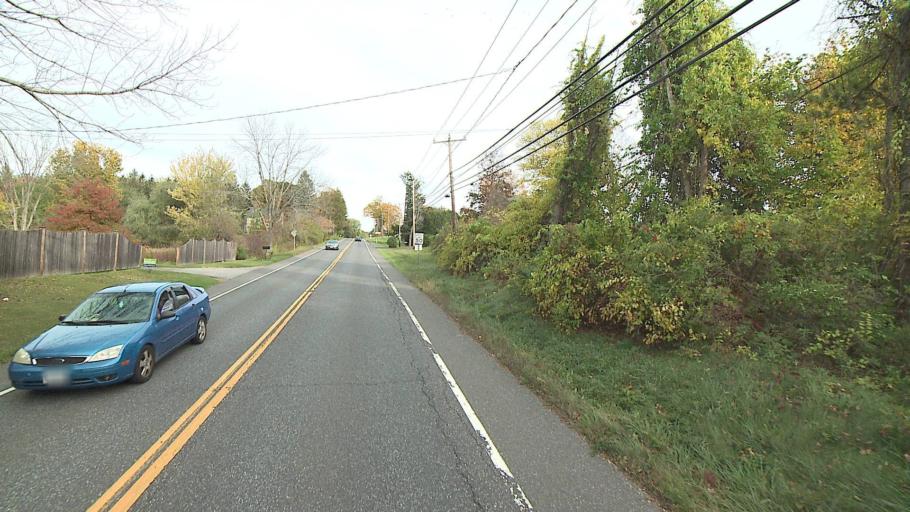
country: US
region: Connecticut
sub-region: Litchfield County
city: Canaan
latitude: 42.0150
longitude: -73.2967
